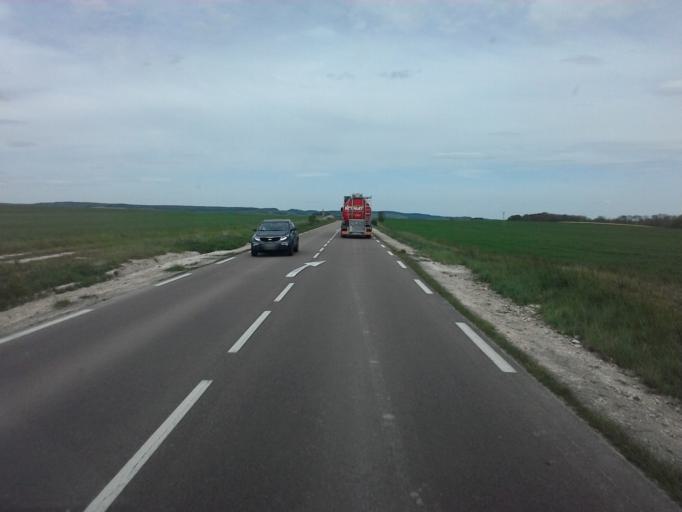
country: FR
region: Bourgogne
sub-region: Departement de l'Yonne
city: Neuvy-Sautour
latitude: 48.0746
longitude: 3.8220
